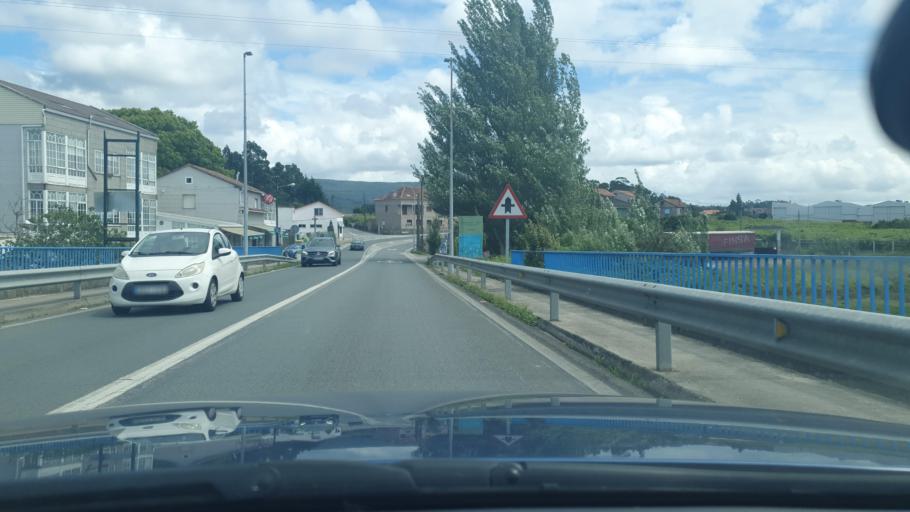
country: ES
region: Galicia
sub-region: Provincia de Pontevedra
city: Cambados
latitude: 42.5005
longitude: -8.8044
